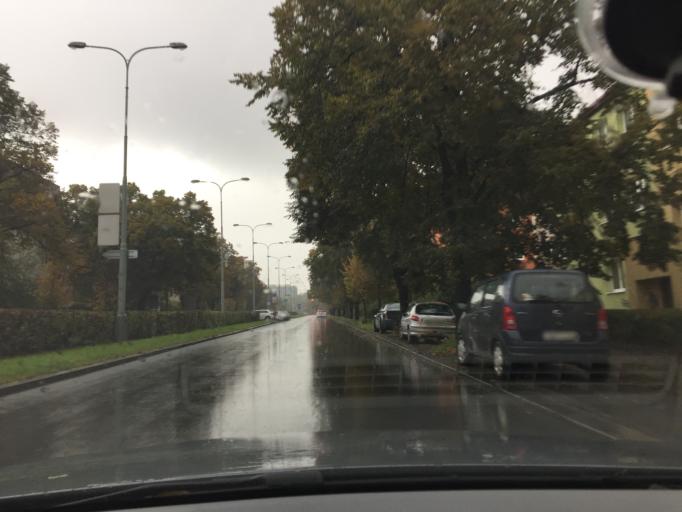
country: CZ
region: Praha
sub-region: Praha 8
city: Liben
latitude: 50.1246
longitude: 14.4522
